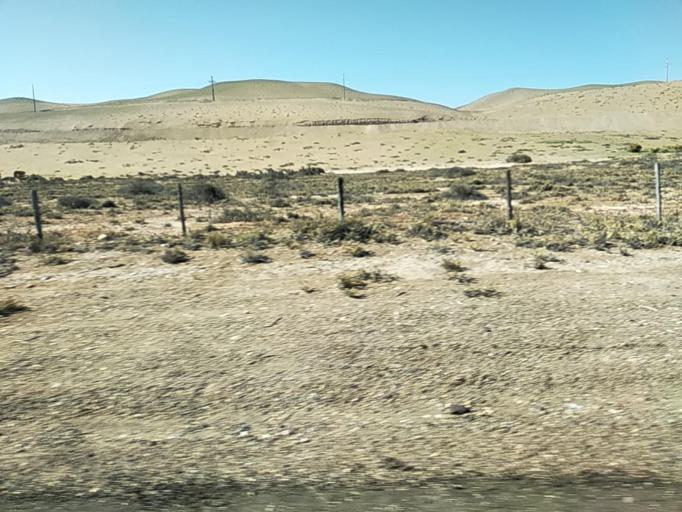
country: CL
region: Atacama
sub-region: Provincia de Copiapo
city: Copiapo
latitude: -27.3415
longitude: -70.7588
